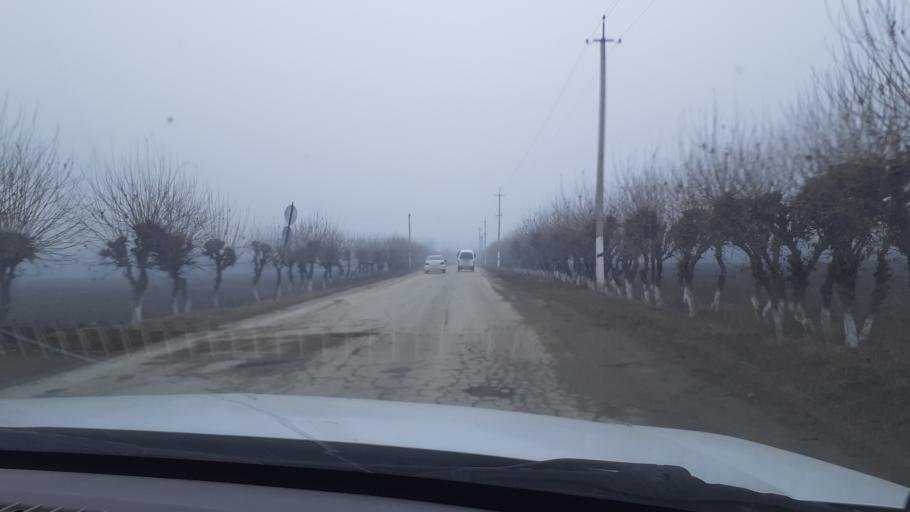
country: UZ
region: Namangan
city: Haqqulobod
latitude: 40.9006
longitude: 71.9986
